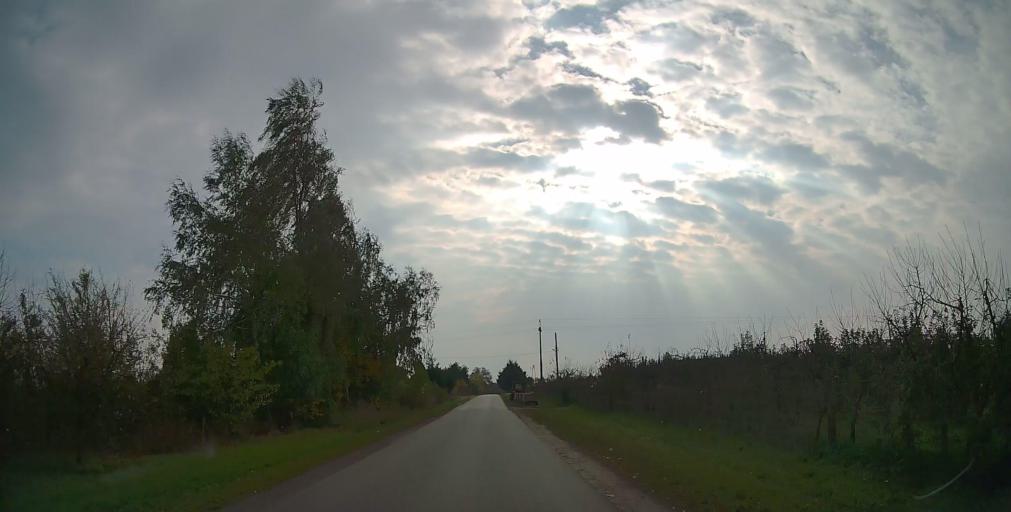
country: PL
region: Masovian Voivodeship
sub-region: Powiat grojecki
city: Mogielnica
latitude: 51.6482
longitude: 20.7314
